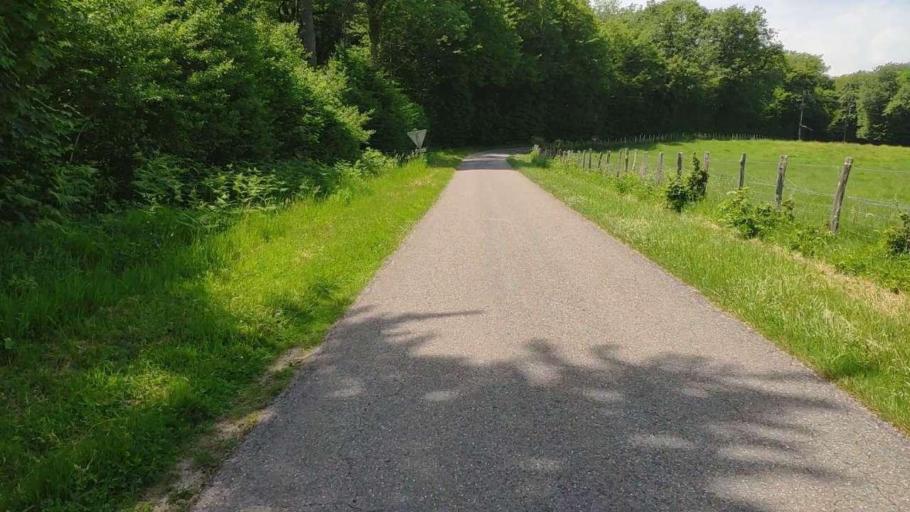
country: FR
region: Franche-Comte
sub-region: Departement du Jura
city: Bletterans
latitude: 46.7715
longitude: 5.4428
